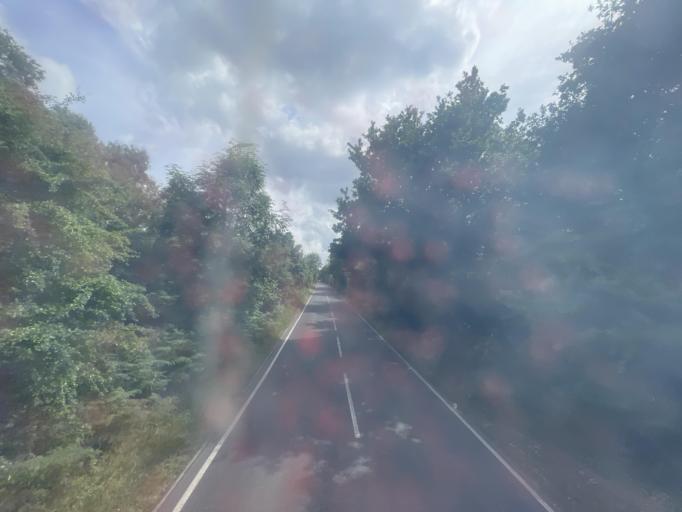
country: GB
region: England
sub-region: Greater London
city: Bromley
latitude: 51.3673
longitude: 0.0251
